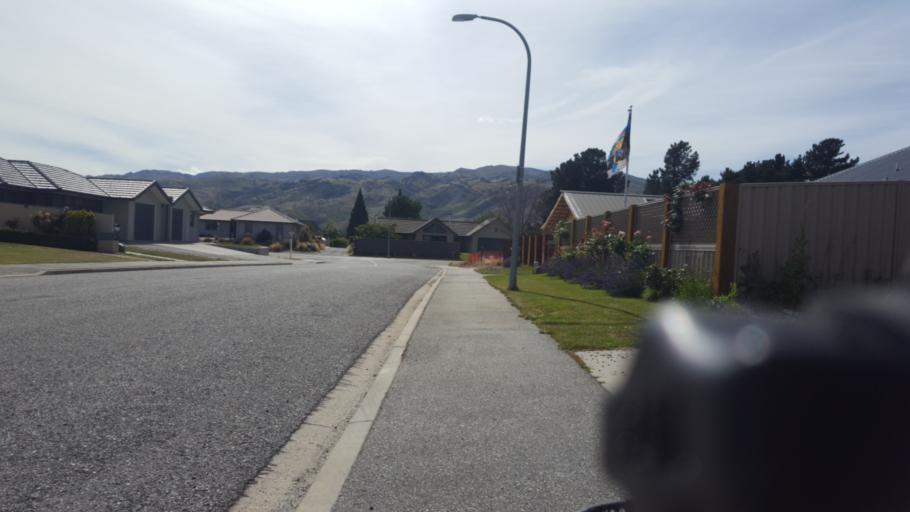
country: NZ
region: Otago
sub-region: Queenstown-Lakes District
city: Wanaka
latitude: -45.0441
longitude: 169.1888
